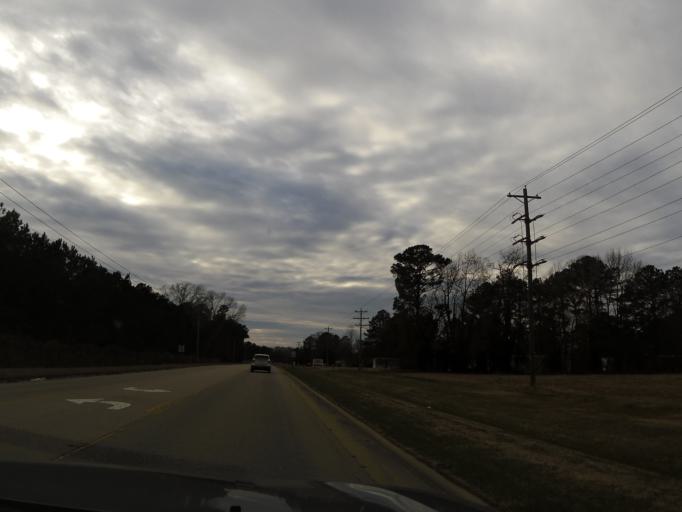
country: US
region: North Carolina
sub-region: Nash County
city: Rocky Mount
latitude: 35.9766
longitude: -77.7409
